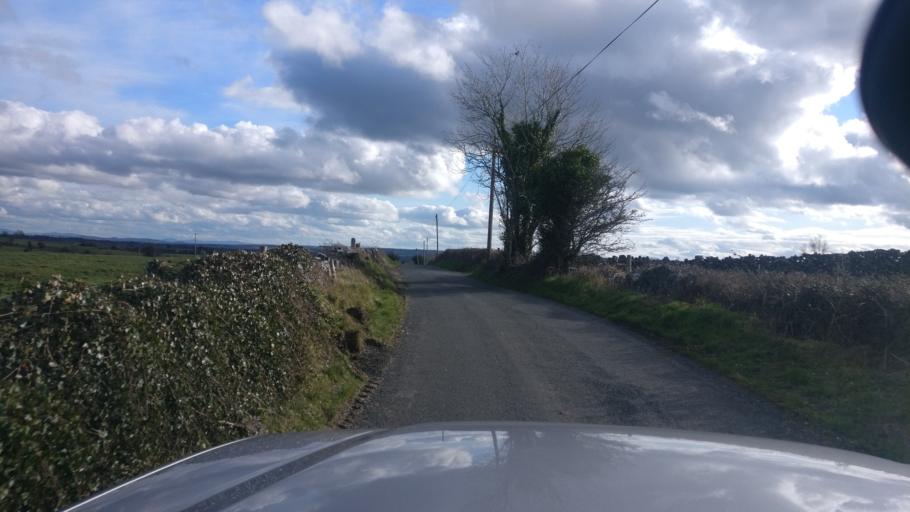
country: IE
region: Connaught
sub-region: County Galway
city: Loughrea
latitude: 53.1737
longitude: -8.4271
